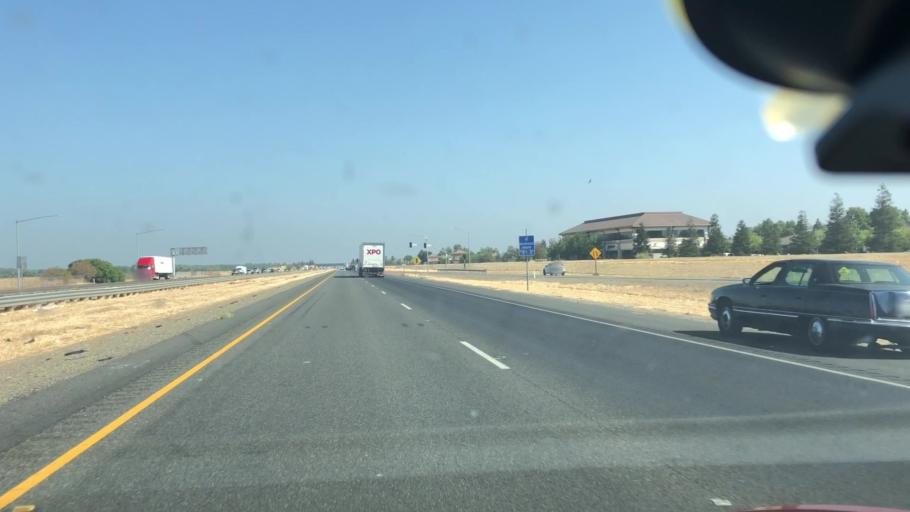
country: US
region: California
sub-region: Sacramento County
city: Laguna
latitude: 38.4112
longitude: -121.4841
